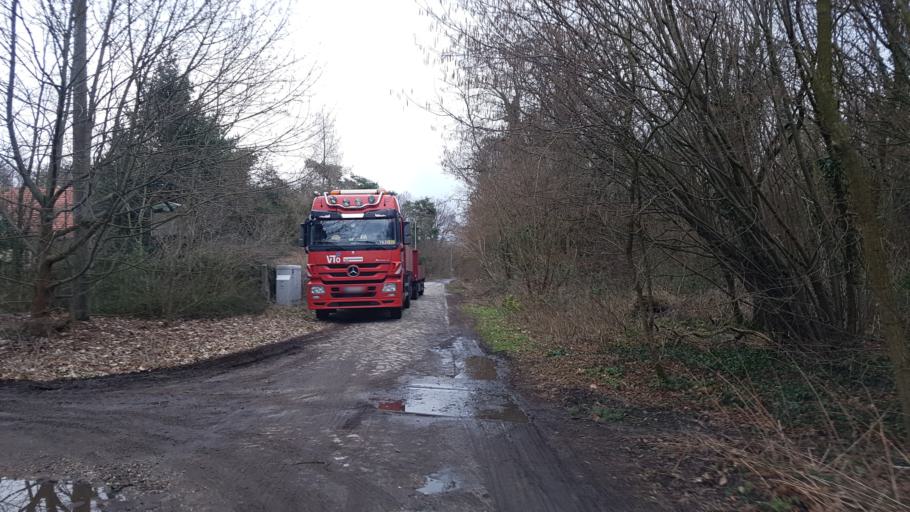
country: DE
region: Brandenburg
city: Plessa
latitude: 51.4737
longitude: 13.5810
